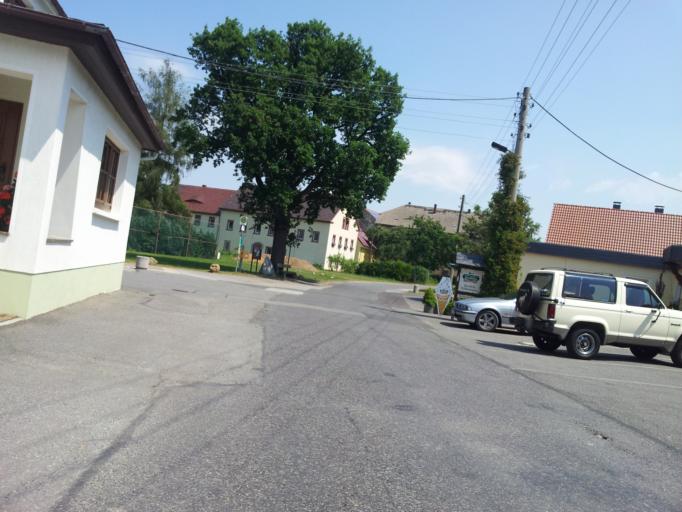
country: DE
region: Saxony
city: Panschwitz-Kuckau
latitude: 51.2084
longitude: 14.2181
